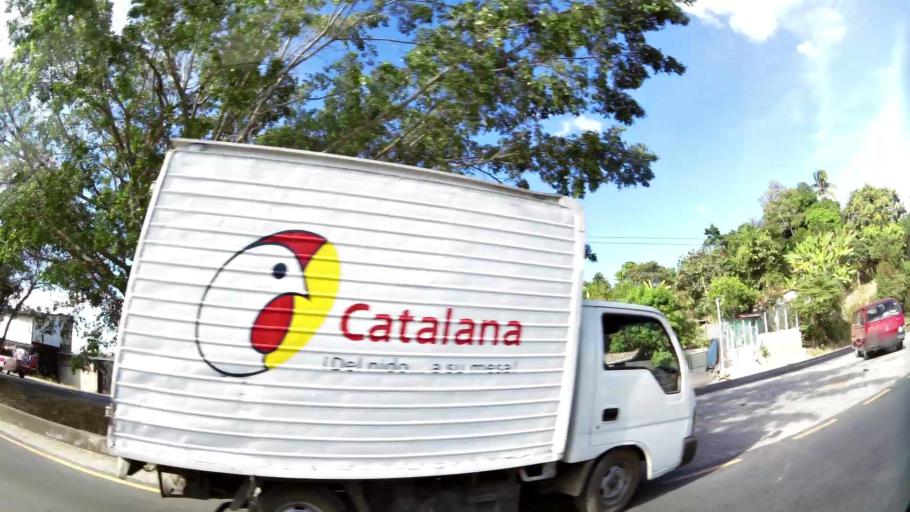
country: SV
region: Cuscatlan
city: Tecoluca
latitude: 13.7367
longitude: -89.0451
